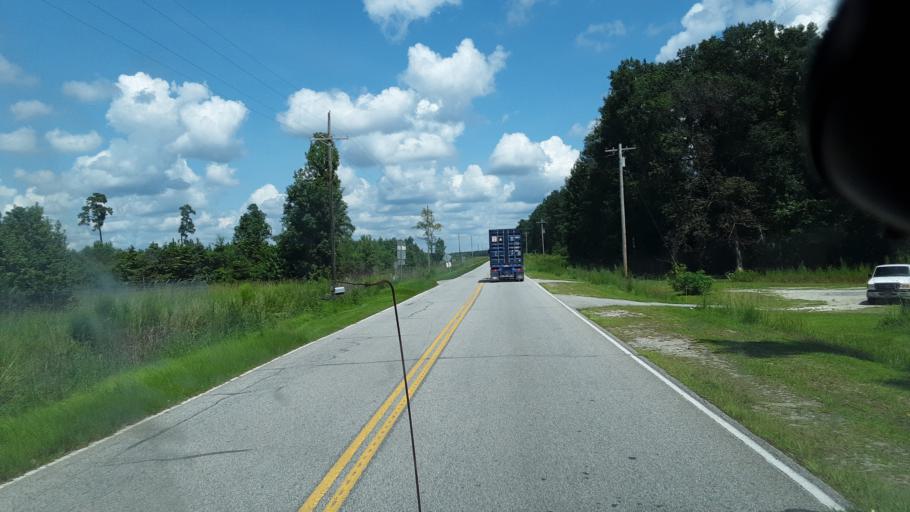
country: US
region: South Carolina
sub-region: Williamsburg County
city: Andrews
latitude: 33.3618
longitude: -79.6516
